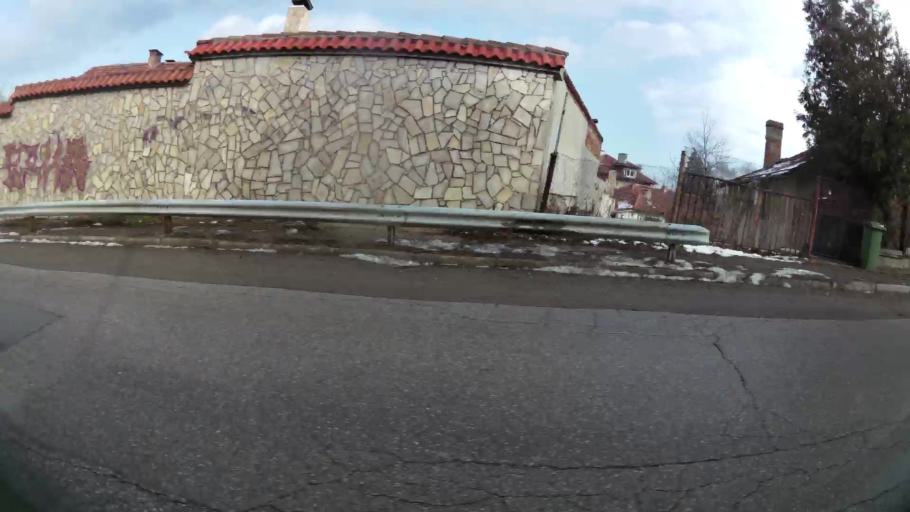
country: BG
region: Sofia-Capital
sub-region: Stolichna Obshtina
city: Sofia
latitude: 42.6476
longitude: 23.2664
